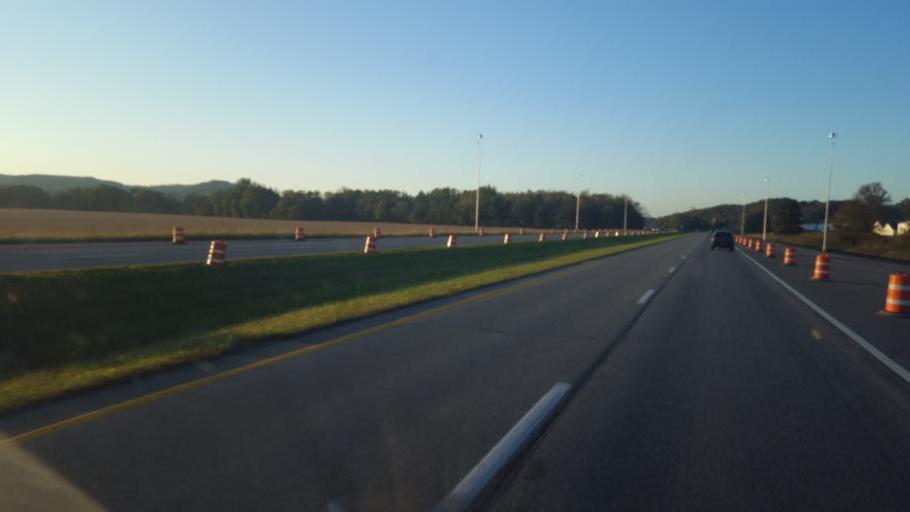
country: US
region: Ohio
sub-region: Scioto County
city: Lucasville
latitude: 38.8969
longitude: -83.0022
